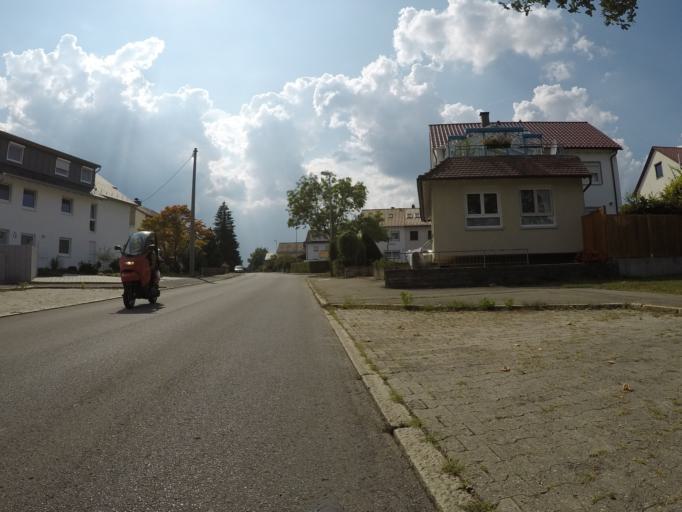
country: DE
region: Baden-Wuerttemberg
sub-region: Tuebingen Region
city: Eningen unter Achalm
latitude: 48.4843
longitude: 9.2478
